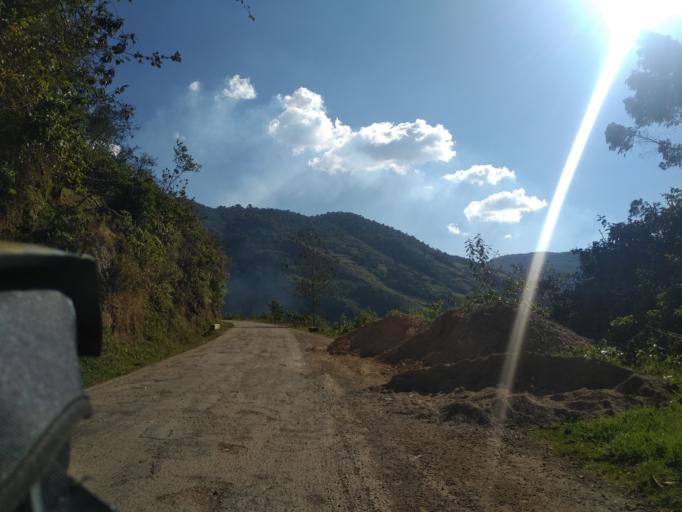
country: PE
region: Amazonas
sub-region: Provincia de Chachapoyas
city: Montevideo
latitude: -6.7151
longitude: -77.8192
